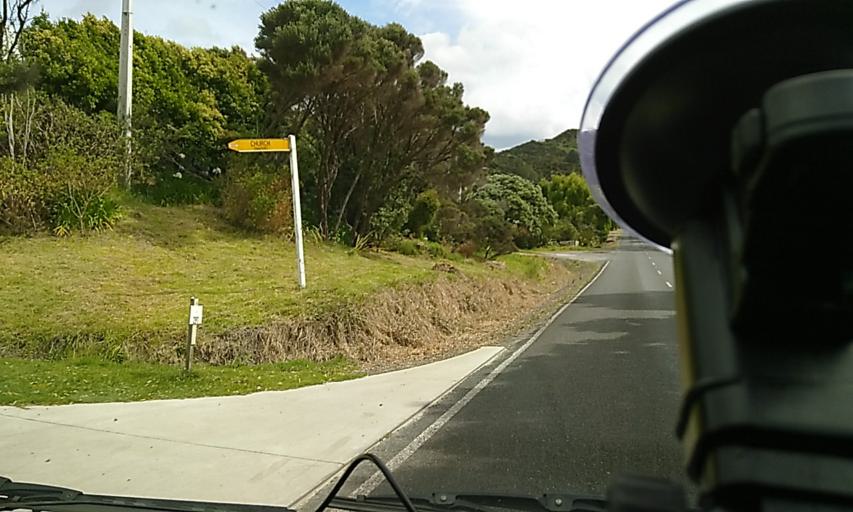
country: NZ
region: Northland
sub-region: Far North District
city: Ahipara
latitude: -35.5326
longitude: 173.3894
